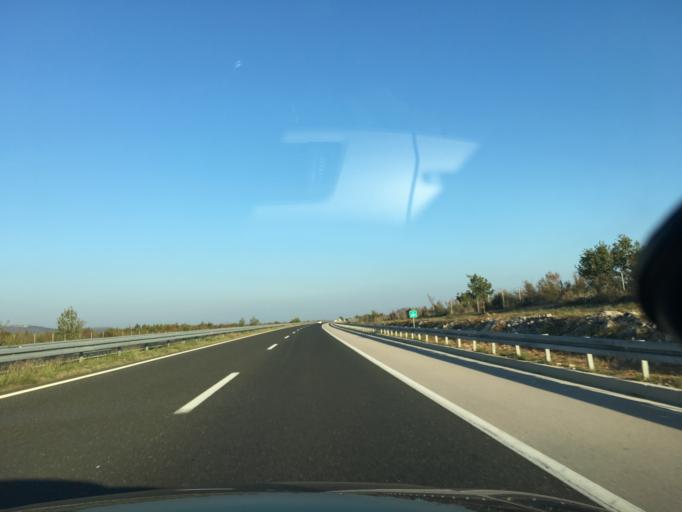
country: HR
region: Sibensko-Kniniska
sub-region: Grad Sibenik
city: Pirovac
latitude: 43.9093
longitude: 15.7552
